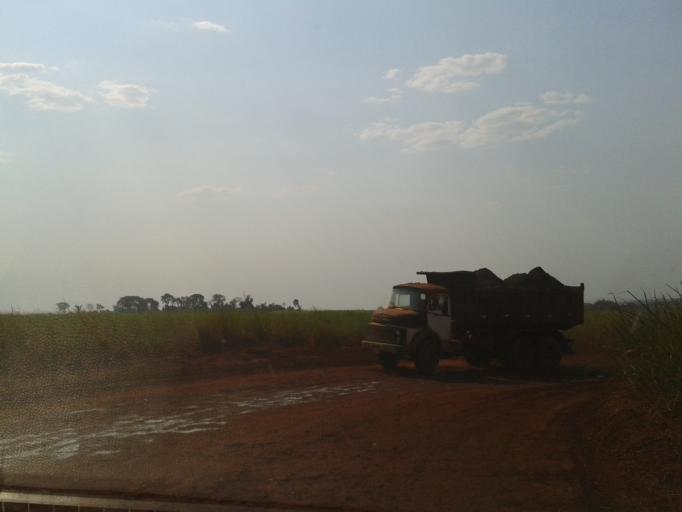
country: BR
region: Minas Gerais
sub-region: Centralina
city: Centralina
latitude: -18.6444
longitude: -49.2438
